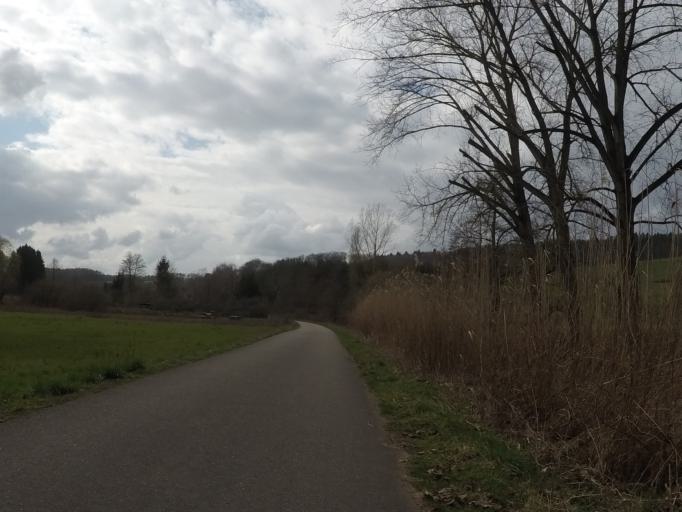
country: DE
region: Rheinland-Pfalz
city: Dellfeld
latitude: 49.2413
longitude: 7.4839
